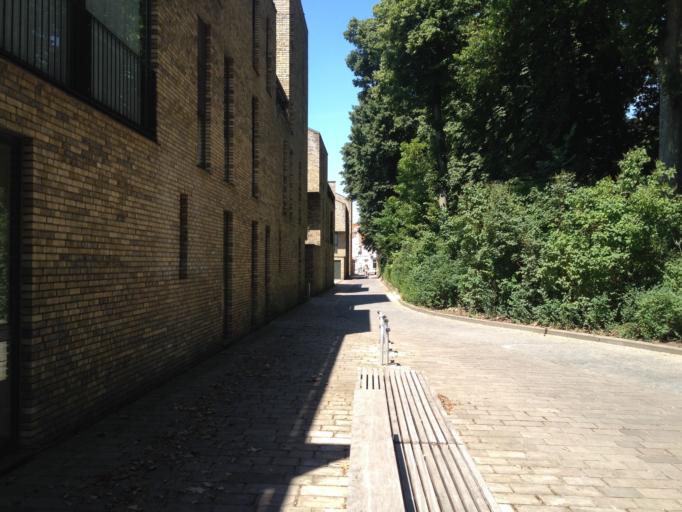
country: BE
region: Flanders
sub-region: Provincie West-Vlaanderen
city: Brugge
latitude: 51.2059
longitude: 3.2307
